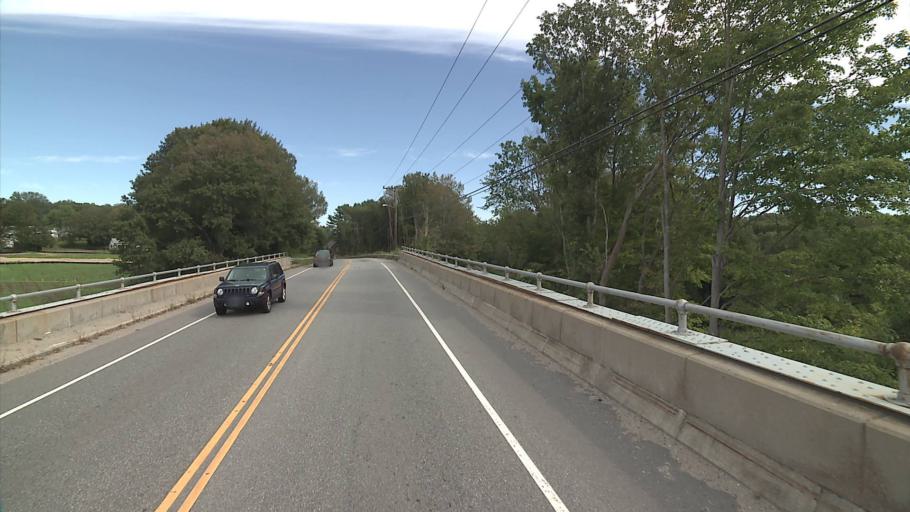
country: US
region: Connecticut
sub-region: Windham County
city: South Windham
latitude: 41.6553
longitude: -72.1582
